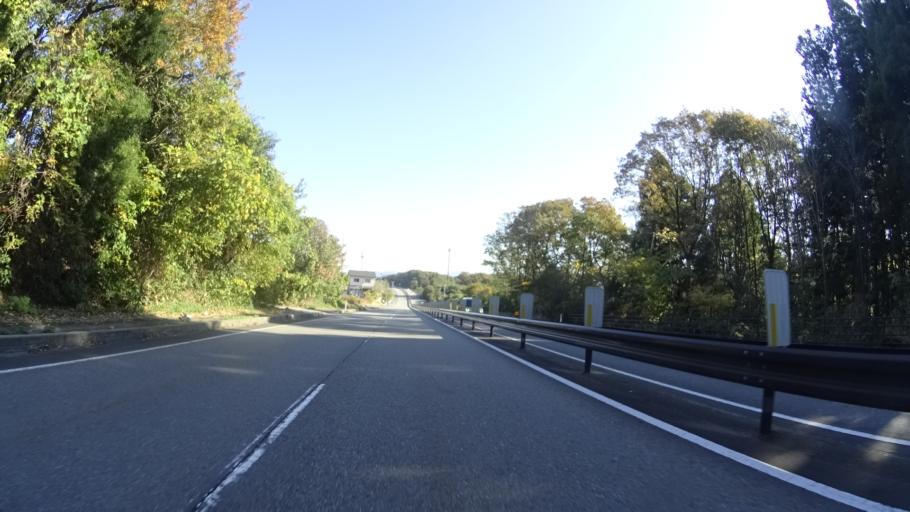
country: JP
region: Ishikawa
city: Komatsu
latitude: 36.3910
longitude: 136.4972
